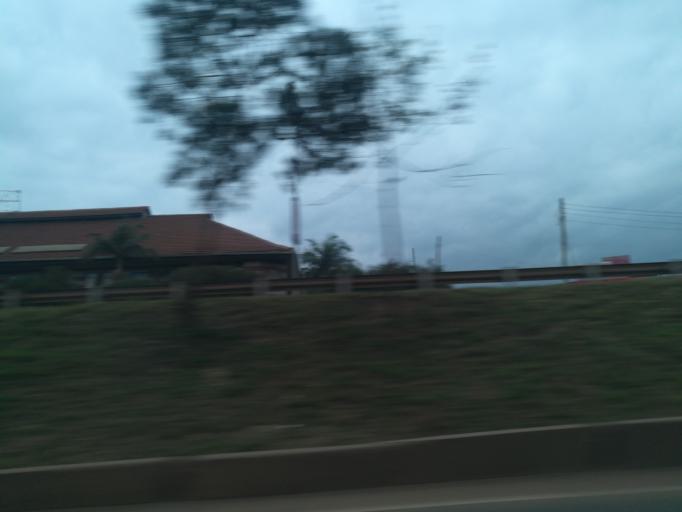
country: KE
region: Nairobi Area
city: Thika
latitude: -1.1060
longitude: 37.0163
